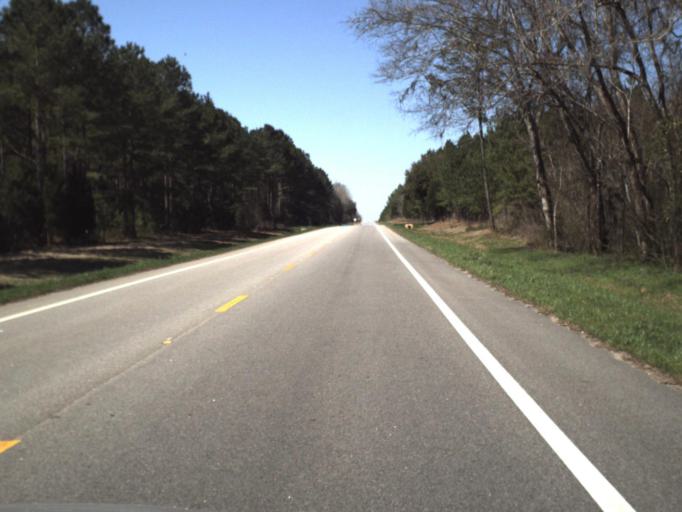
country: US
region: Florida
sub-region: Jackson County
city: Marianna
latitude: 30.8269
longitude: -85.3310
